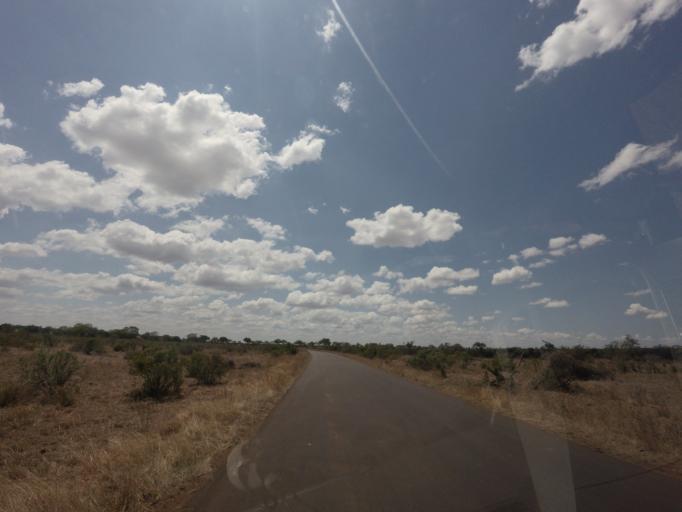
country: ZA
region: Limpopo
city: Thulamahashi
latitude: -24.3954
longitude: 31.7854
